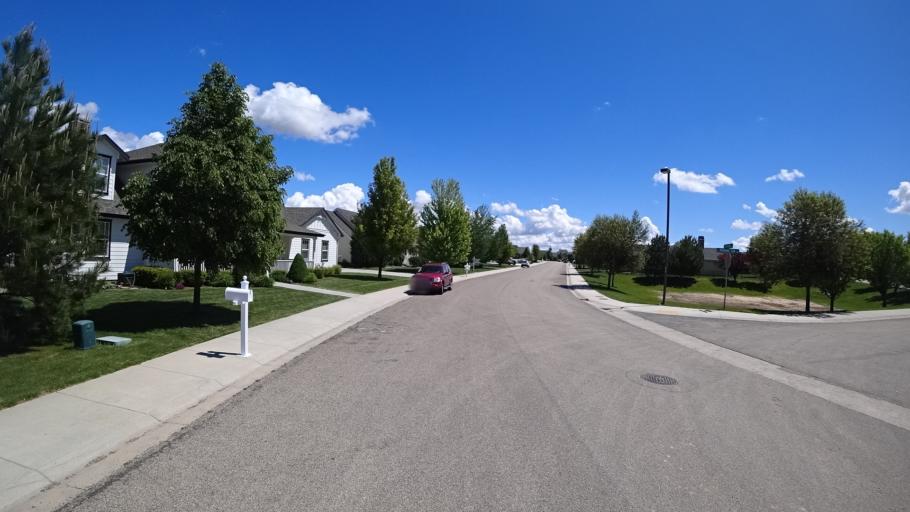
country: US
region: Idaho
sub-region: Ada County
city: Kuna
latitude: 43.5132
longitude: -116.4322
